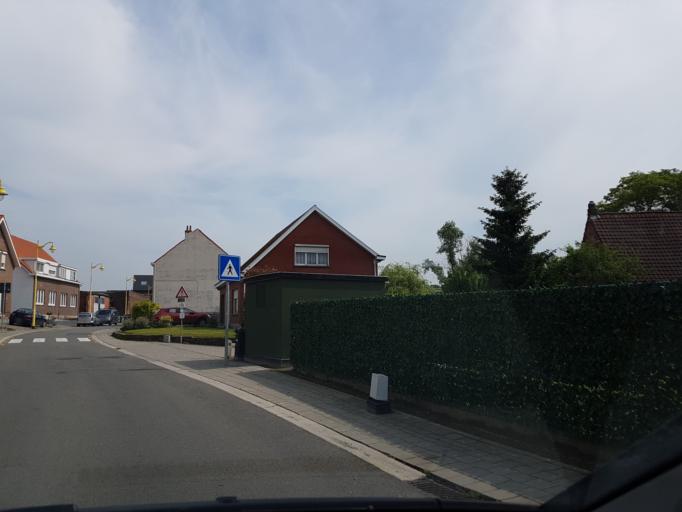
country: BE
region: Flanders
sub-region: Provincie Vlaams-Brabant
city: Meise
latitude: 50.9503
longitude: 4.3047
